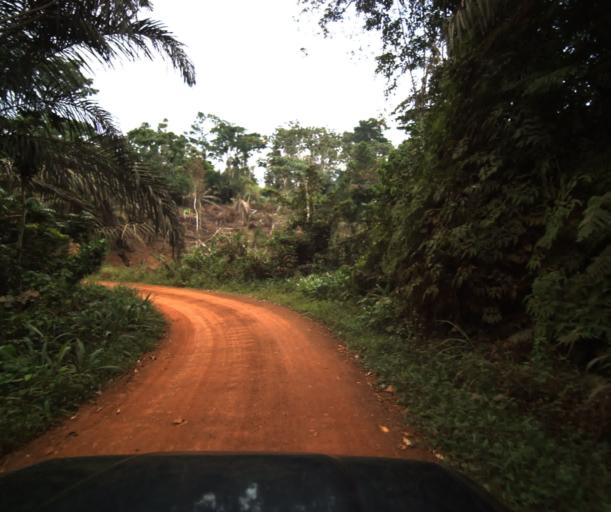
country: CM
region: Centre
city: Akono
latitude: 3.5937
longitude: 11.1666
